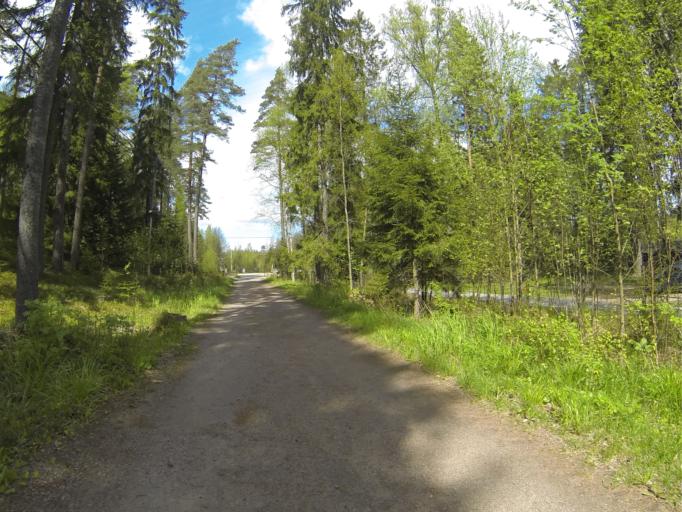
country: FI
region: Varsinais-Suomi
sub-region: Salo
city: Halikko
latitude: 60.3006
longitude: 23.0771
